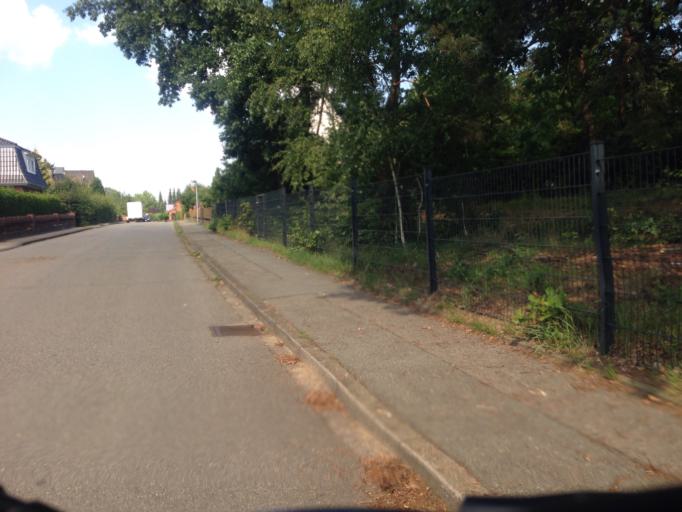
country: DE
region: Lower Saxony
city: Adendorf
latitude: 53.2772
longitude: 10.4327
